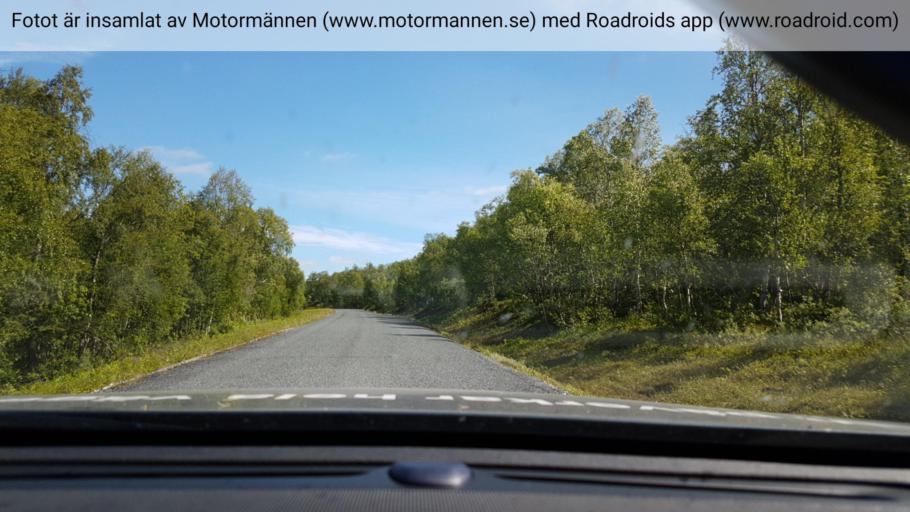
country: NO
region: Nordland
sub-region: Hattfjelldal
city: Hattfjelldal
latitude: 65.4197
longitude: 14.8730
